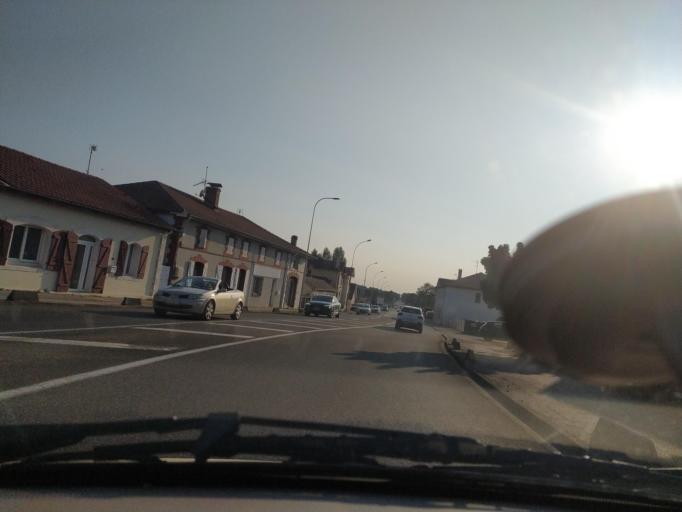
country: FR
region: Aquitaine
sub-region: Departement des Landes
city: Saint-Geours-de-Maremne
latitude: 43.6875
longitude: -1.2299
